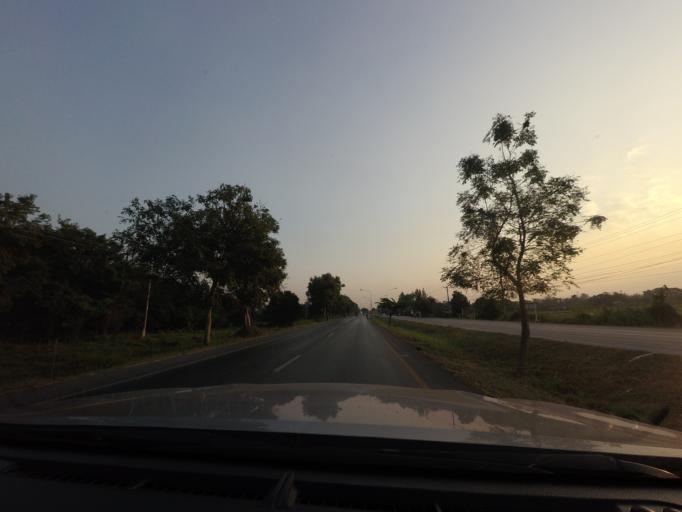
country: TH
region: Phitsanulok
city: Wang Thong
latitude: 16.7324
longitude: 100.4316
